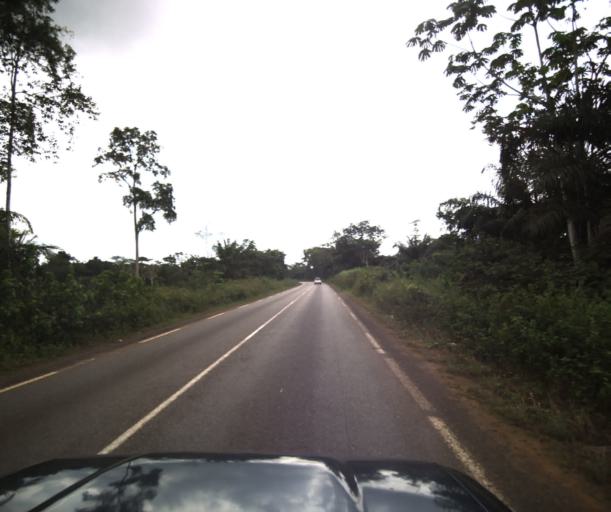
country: CM
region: Littoral
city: Edea
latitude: 3.8077
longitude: 10.2832
